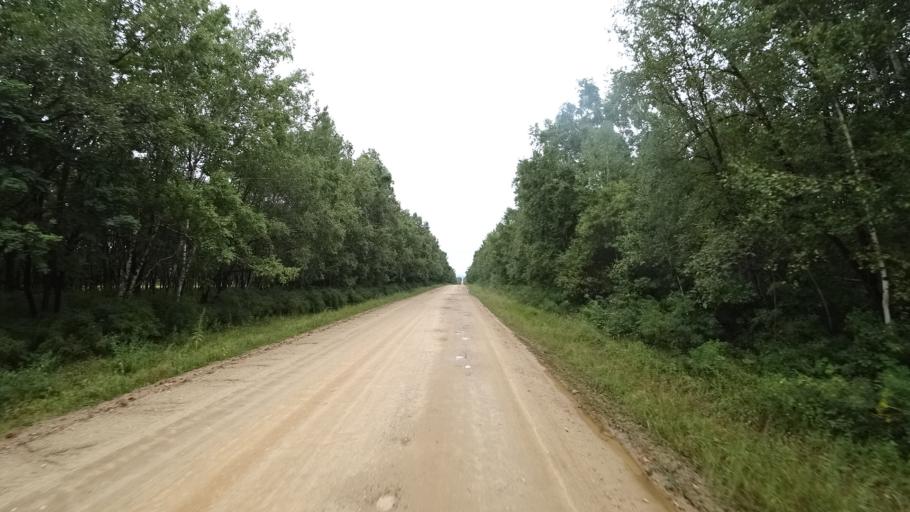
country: RU
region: Primorskiy
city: Ivanovka
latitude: 44.0319
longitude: 132.5308
